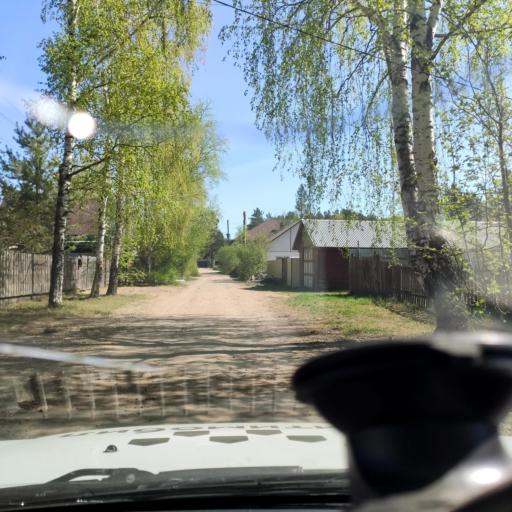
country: RU
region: Perm
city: Perm
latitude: 58.0508
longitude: 56.2790
